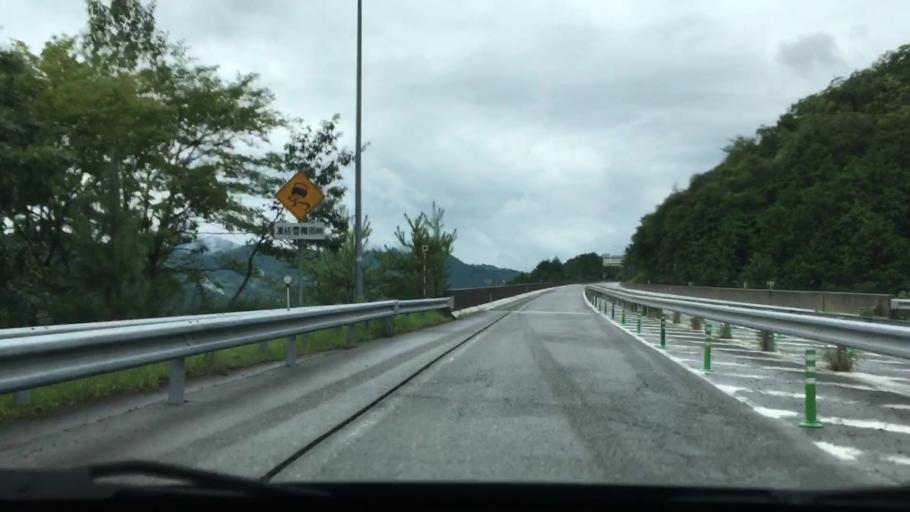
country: JP
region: Hyogo
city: Toyooka
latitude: 35.2847
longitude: 134.8214
